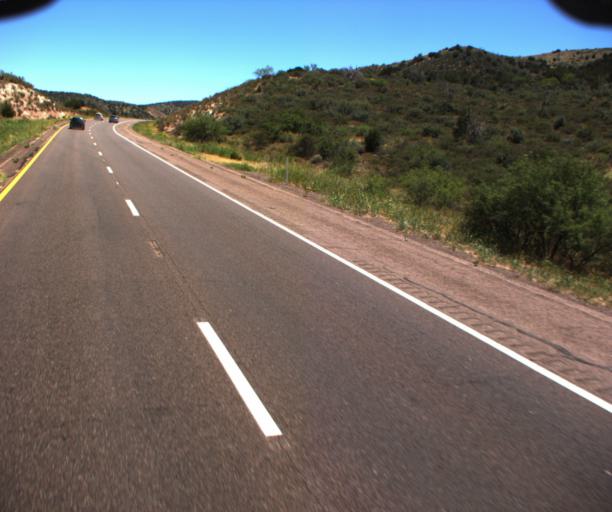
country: US
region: Arizona
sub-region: Gila County
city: Tonto Basin
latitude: 34.0235
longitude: -111.3617
